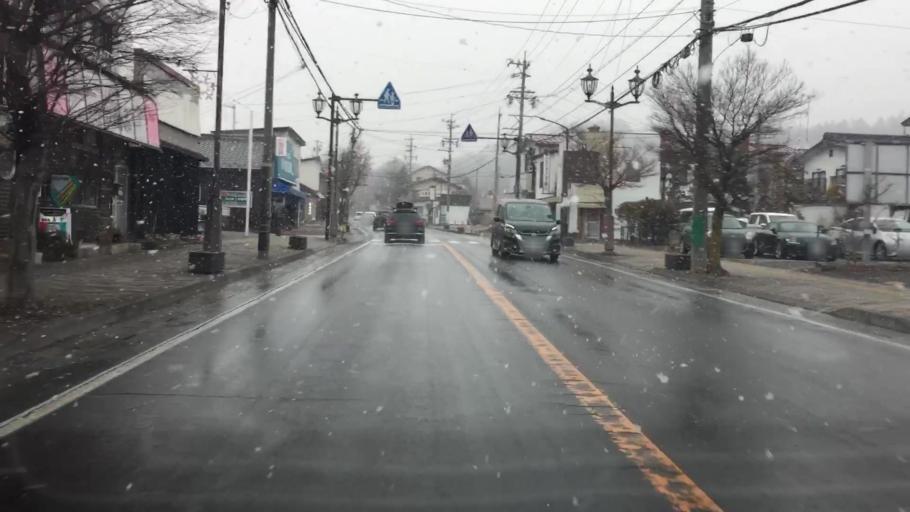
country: JP
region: Nagano
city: Komoro
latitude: 36.3505
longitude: 138.5915
